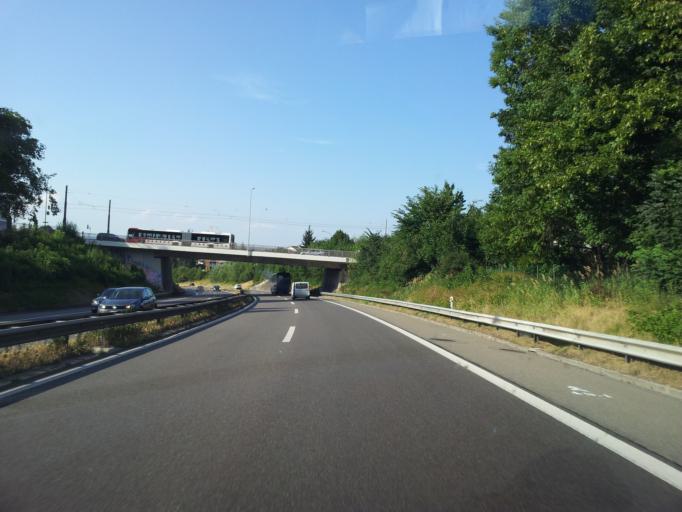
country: CH
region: Fribourg
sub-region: Sarine District
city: Givisiez
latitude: 46.8104
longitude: 7.1384
